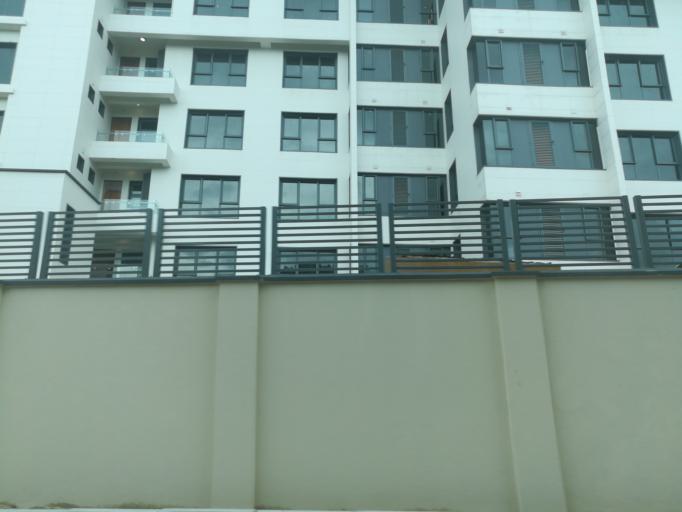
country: NG
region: Lagos
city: Lagos
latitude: 6.4398
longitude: 3.4101
